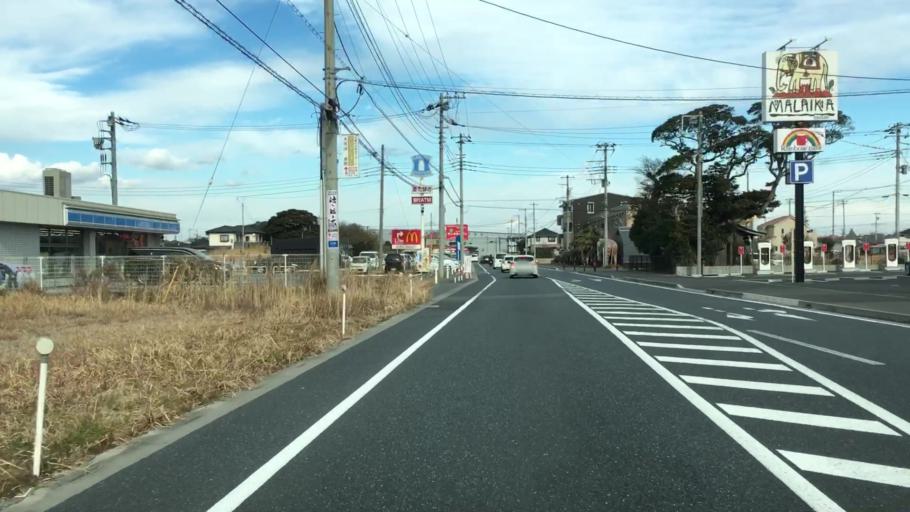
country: JP
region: Chiba
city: Kisarazu
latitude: 35.4355
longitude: 139.9241
